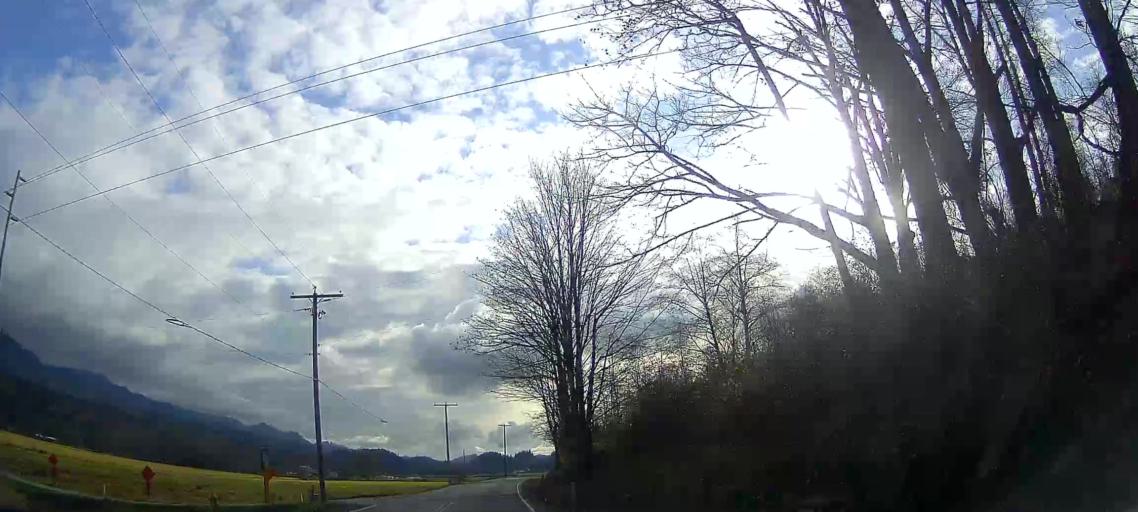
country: US
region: Washington
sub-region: Skagit County
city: Clear Lake
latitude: 48.4427
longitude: -122.2197
